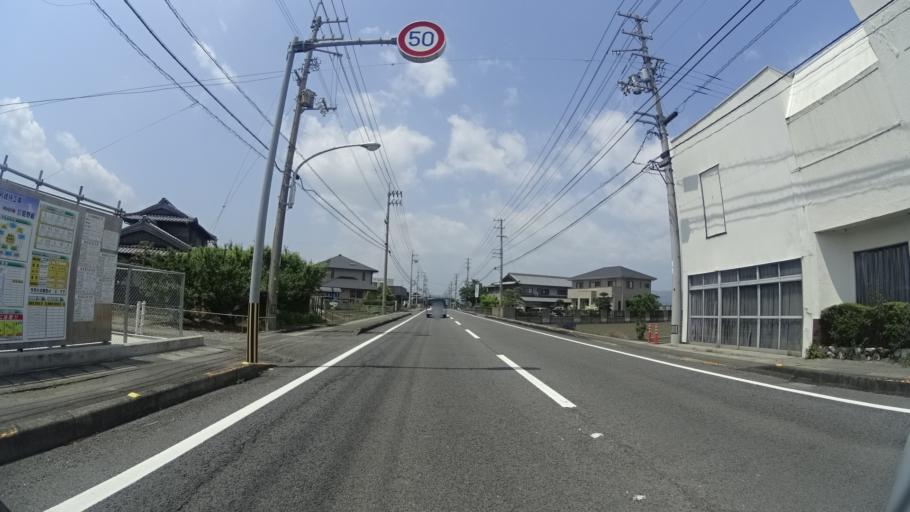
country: JP
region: Tokushima
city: Ishii
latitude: 34.0678
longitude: 134.4151
